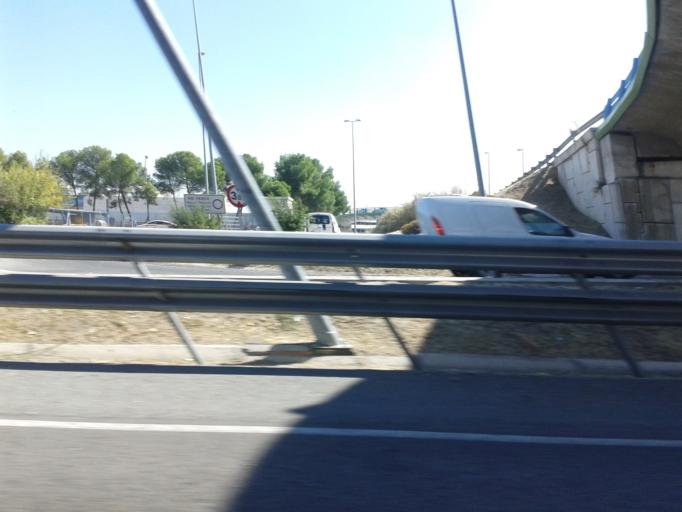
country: ES
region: Madrid
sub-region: Provincia de Madrid
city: Barajas de Madrid
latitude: 40.4707
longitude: -3.5747
